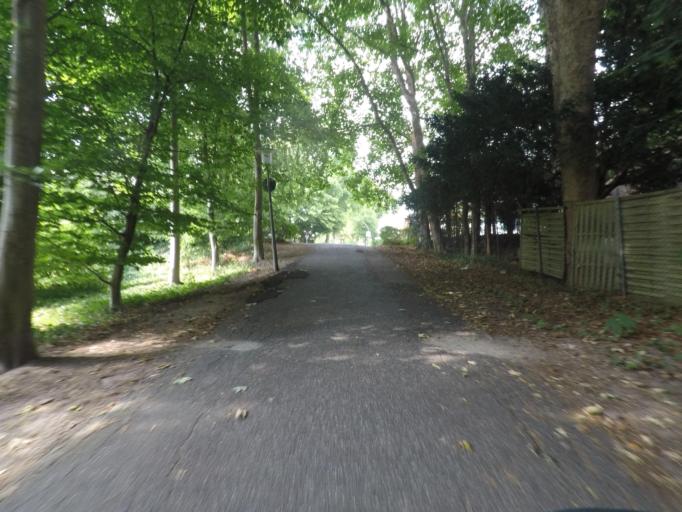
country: DE
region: Hamburg
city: Wellingsbuettel
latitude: 53.6429
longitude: 10.0659
